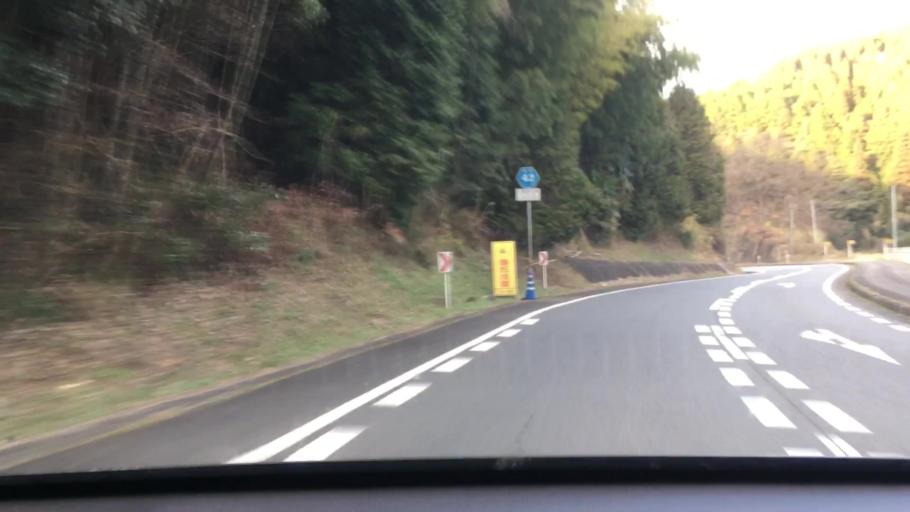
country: JP
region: Oita
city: Hiji
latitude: 33.4244
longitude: 131.4135
